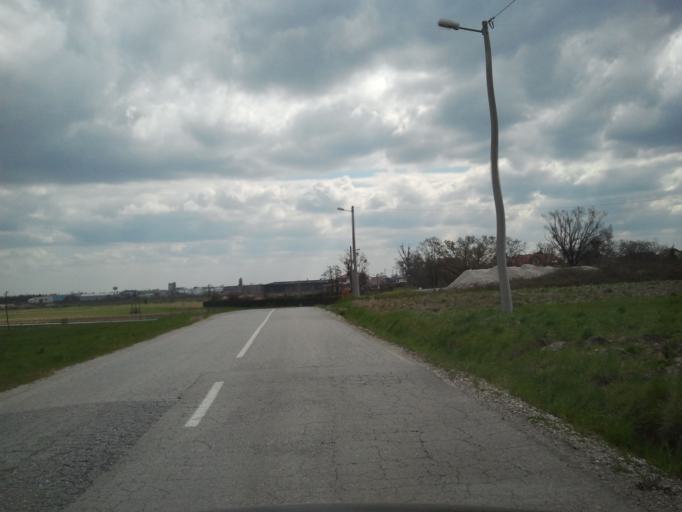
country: HR
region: Grad Zagreb
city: Lucko
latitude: 45.7488
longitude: 15.8590
